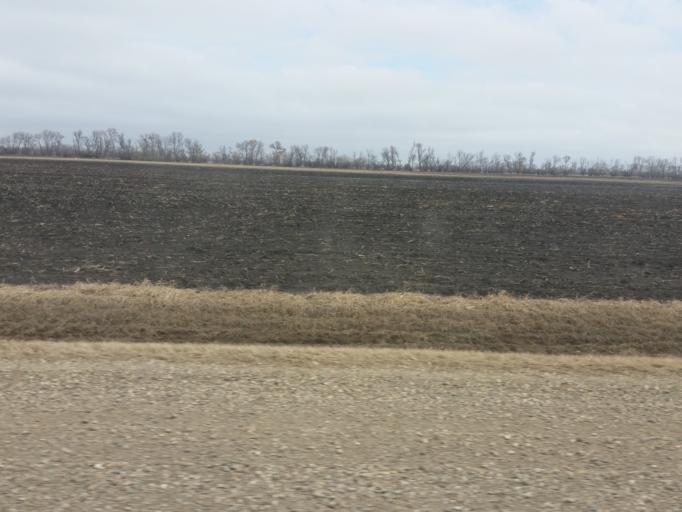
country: US
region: North Dakota
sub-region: Walsh County
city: Grafton
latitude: 48.4229
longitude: -97.3212
